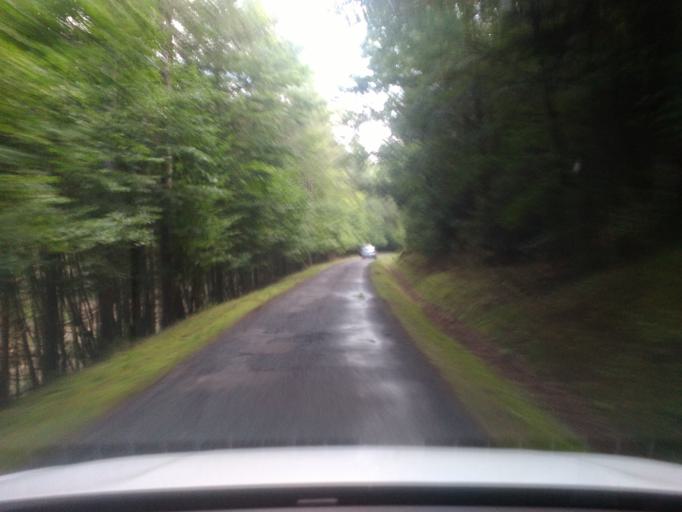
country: FR
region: Lorraine
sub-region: Departement des Vosges
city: Moyenmoutier
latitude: 48.4016
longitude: 6.9068
